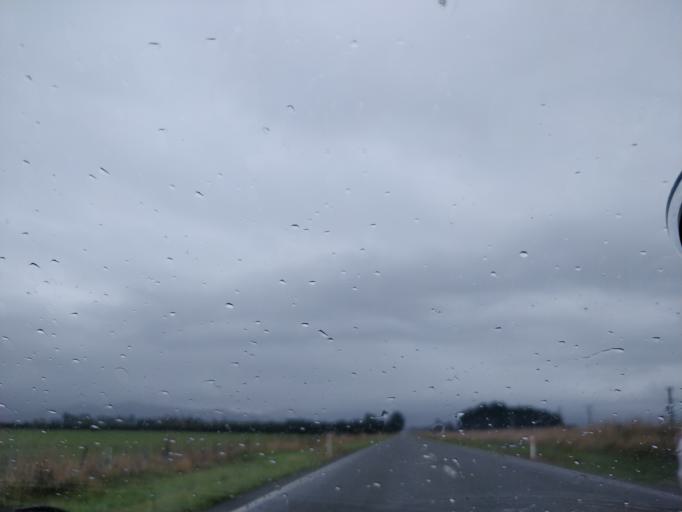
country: NZ
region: Canterbury
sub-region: Selwyn District
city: Darfield
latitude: -43.3821
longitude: 172.0075
